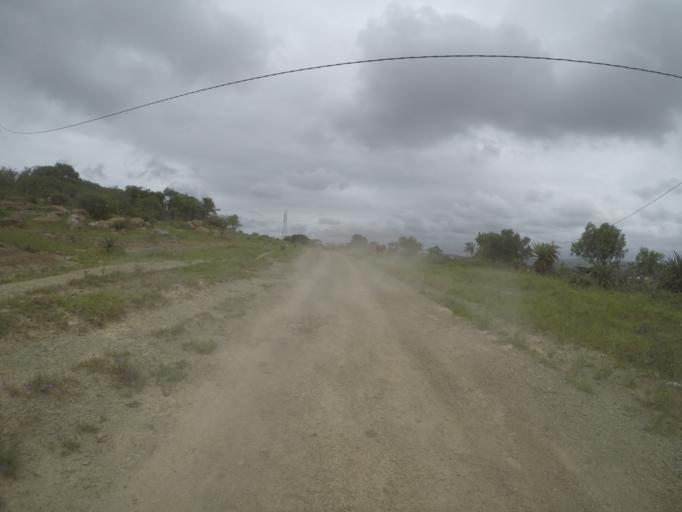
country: ZA
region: KwaZulu-Natal
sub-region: uThungulu District Municipality
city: Empangeni
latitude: -28.5996
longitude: 31.8480
